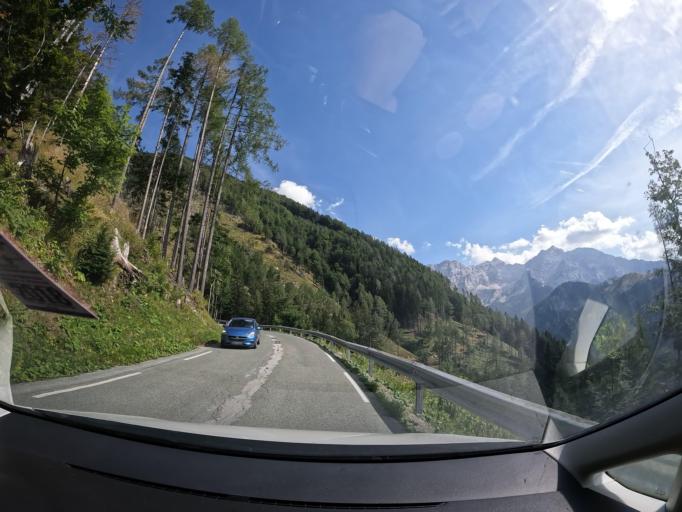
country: AT
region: Carinthia
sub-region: Politischer Bezirk Sankt Veit an der Glan
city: Liebenfels
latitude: 46.7062
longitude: 14.2855
